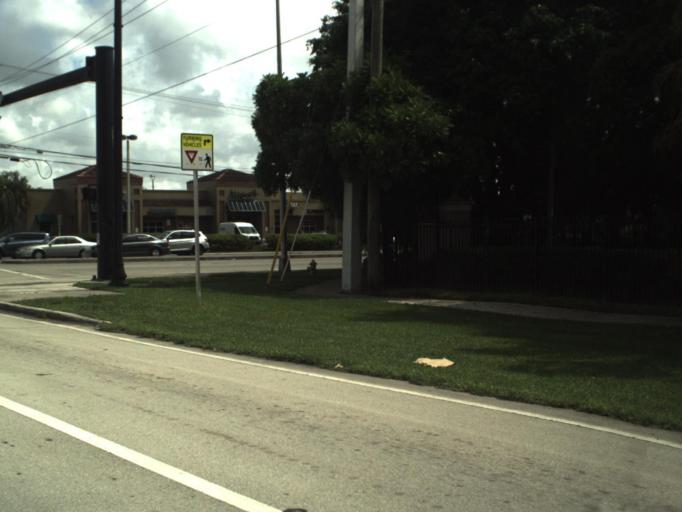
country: US
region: Florida
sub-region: Miami-Dade County
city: Country Club
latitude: 25.9927
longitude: -80.3114
